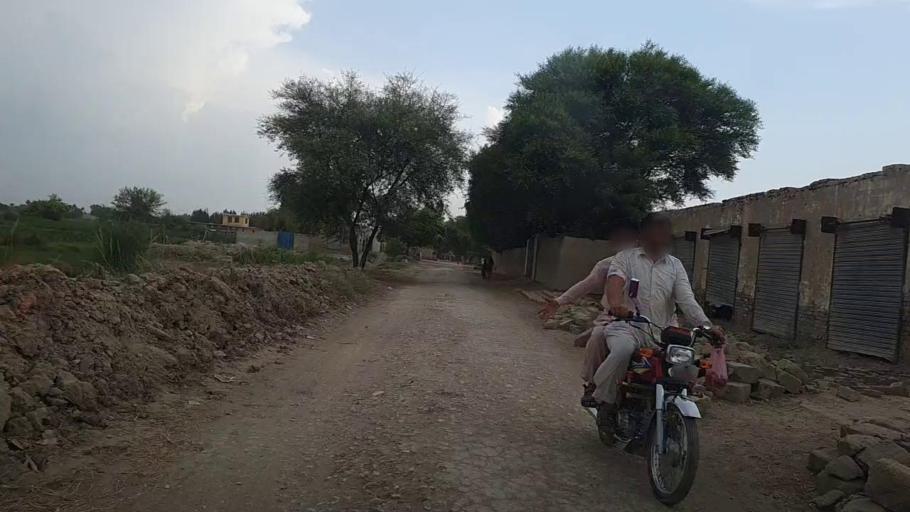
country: PK
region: Sindh
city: Khanpur
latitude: 27.8530
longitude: 69.4861
